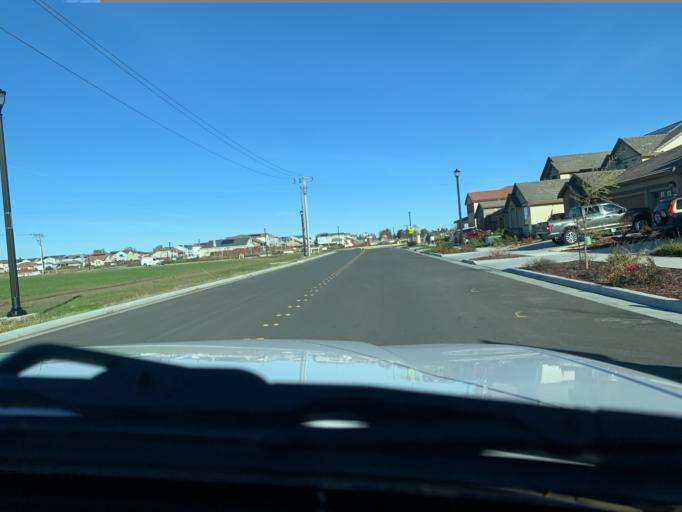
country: US
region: California
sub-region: Yolo County
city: Woodland
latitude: 38.6542
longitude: -121.7473
